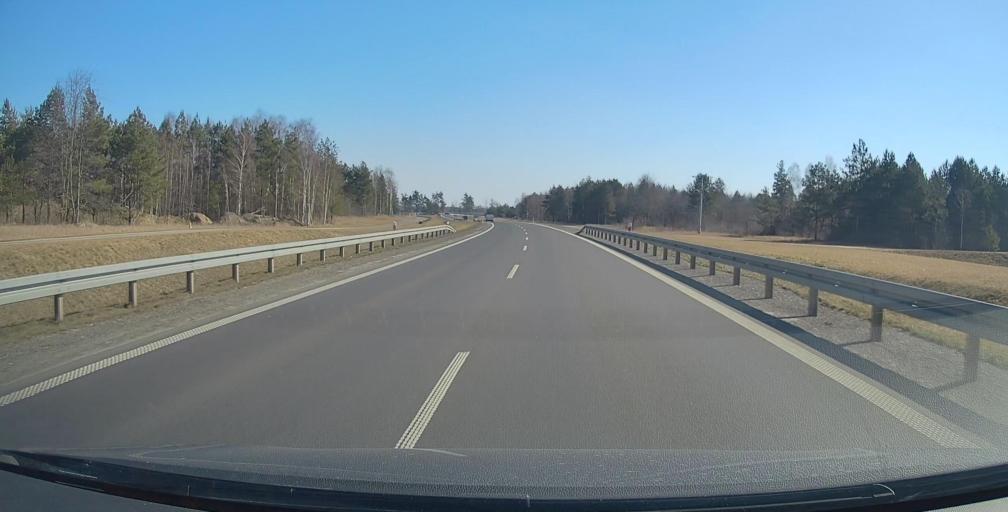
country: PL
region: Subcarpathian Voivodeship
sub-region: Powiat nizanski
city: Raclawice
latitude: 50.4957
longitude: 22.1858
